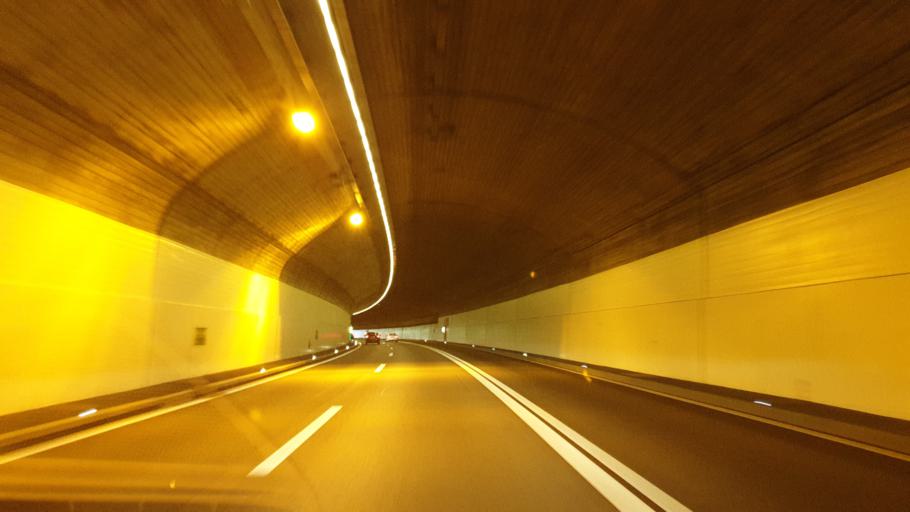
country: CH
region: Zurich
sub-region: Bezirk Dietikon
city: Dietikon / Hofacker
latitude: 47.3891
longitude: 8.4141
